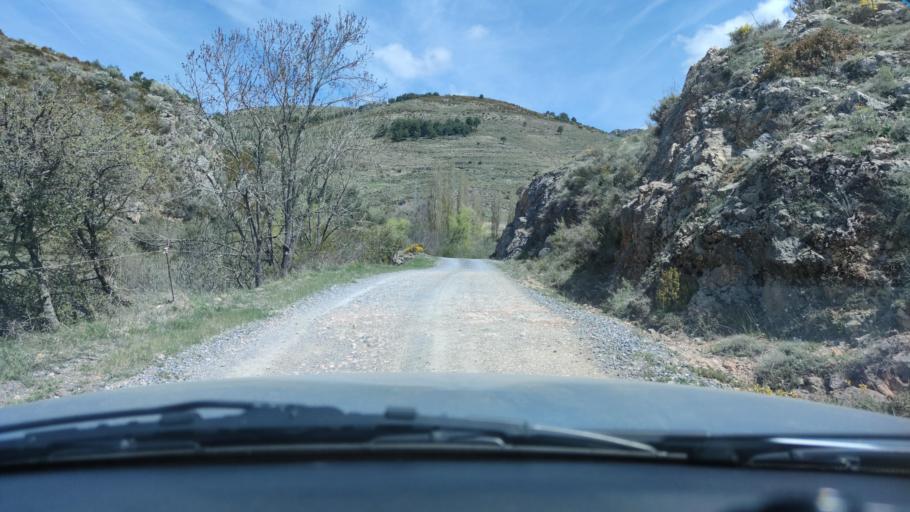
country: ES
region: Catalonia
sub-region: Provincia de Lleida
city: Sort
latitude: 42.2922
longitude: 1.1878
